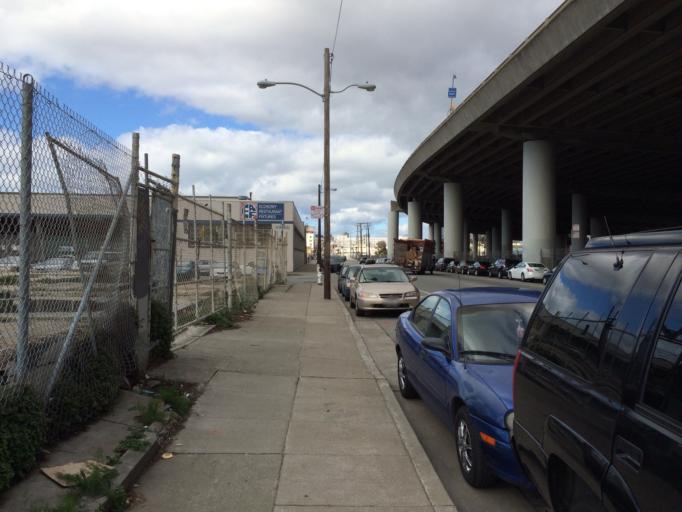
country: US
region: California
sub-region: San Francisco County
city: San Francisco
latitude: 37.7675
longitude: -122.3964
